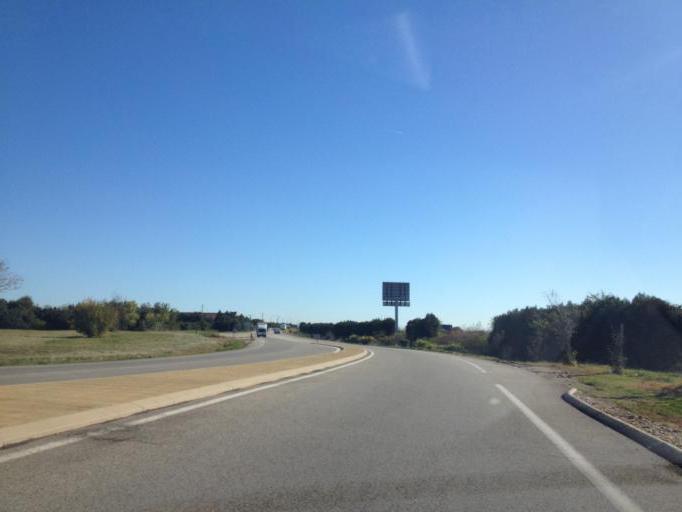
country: FR
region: Provence-Alpes-Cote d'Azur
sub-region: Departement du Vaucluse
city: Courthezon
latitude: 44.0997
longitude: 4.8667
